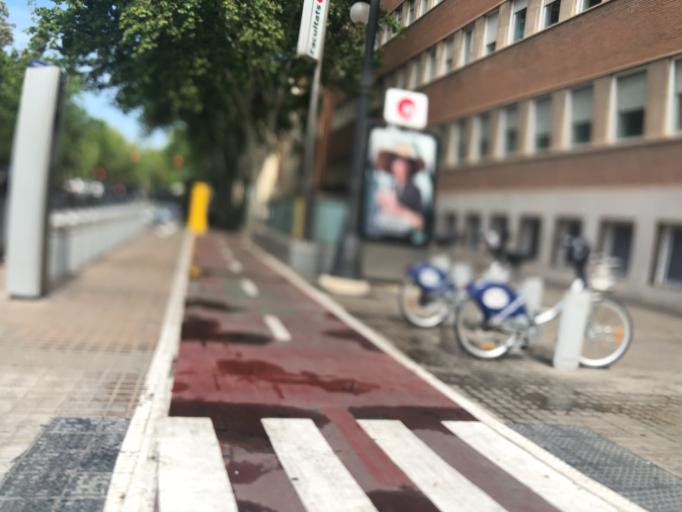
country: ES
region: Valencia
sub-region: Provincia de Valencia
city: Valencia
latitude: 39.4784
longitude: -0.3619
